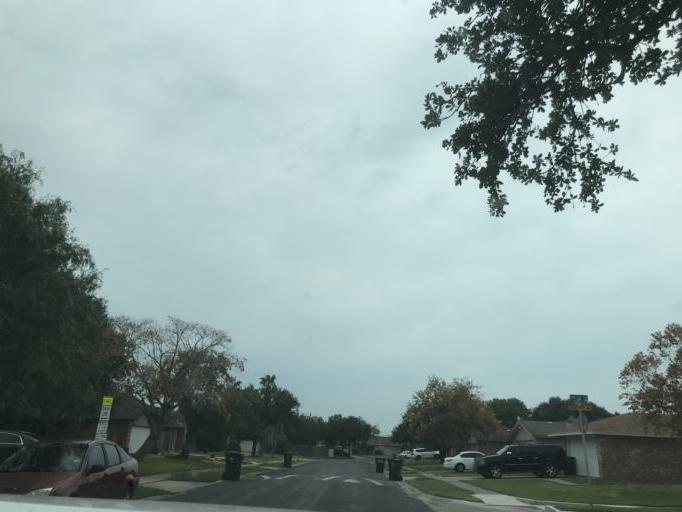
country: US
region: Texas
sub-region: Nueces County
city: Corpus Christi
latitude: 27.6720
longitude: -97.3486
